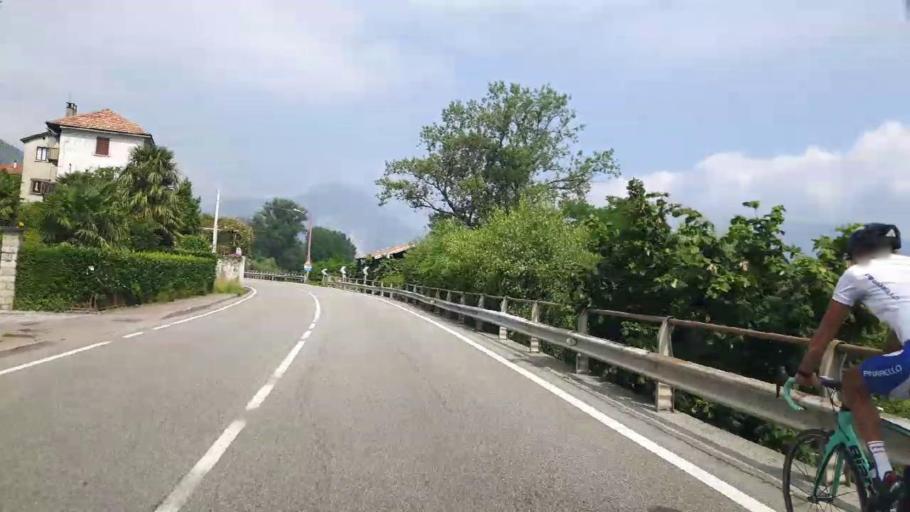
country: IT
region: Piedmont
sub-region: Provincia Verbano-Cusio-Ossola
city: Baveno
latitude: 45.9160
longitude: 8.5014
